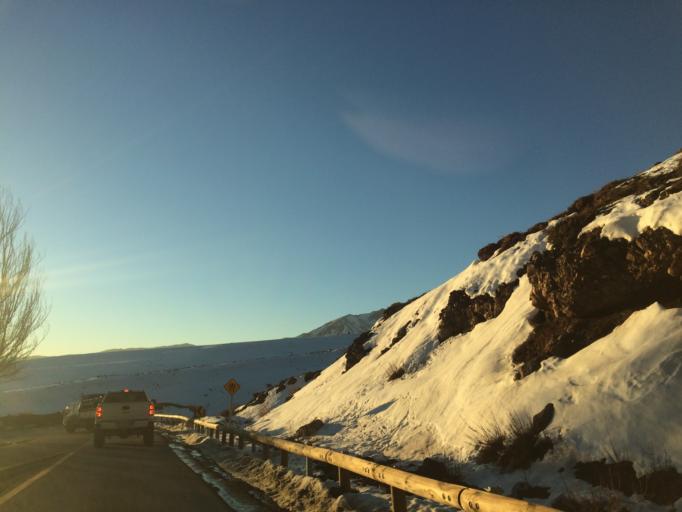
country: CL
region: Santiago Metropolitan
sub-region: Provincia de Santiago
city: Villa Presidente Frei, Nunoa, Santiago, Chile
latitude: -33.3404
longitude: -70.2937
